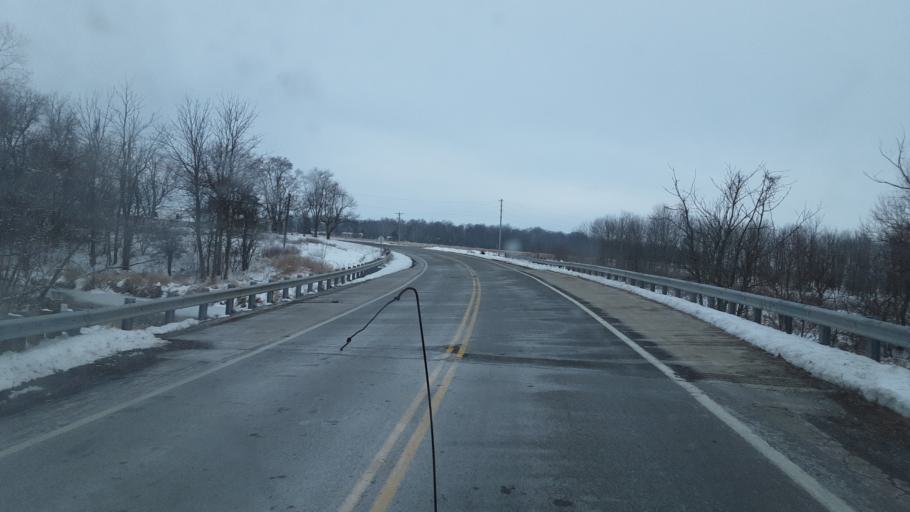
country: US
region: Ohio
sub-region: Champaign County
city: Mechanicsburg
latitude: 40.1221
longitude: -83.4551
